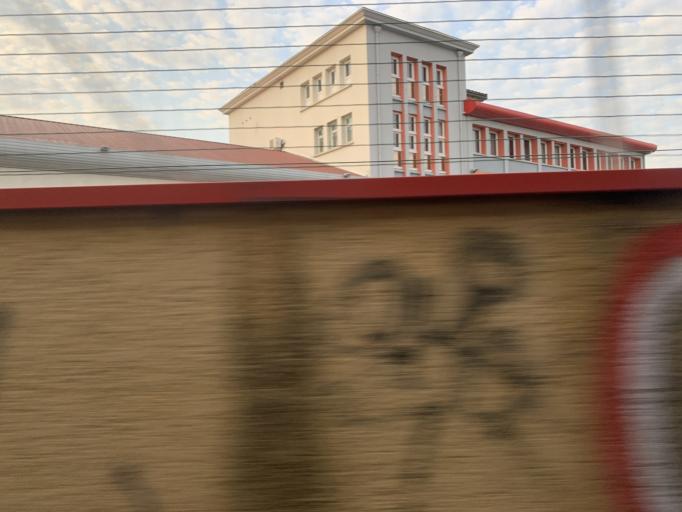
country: FR
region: Rhone-Alpes
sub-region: Departement du Rhone
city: Vaulx-en-Velin
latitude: 45.7666
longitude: 4.9441
